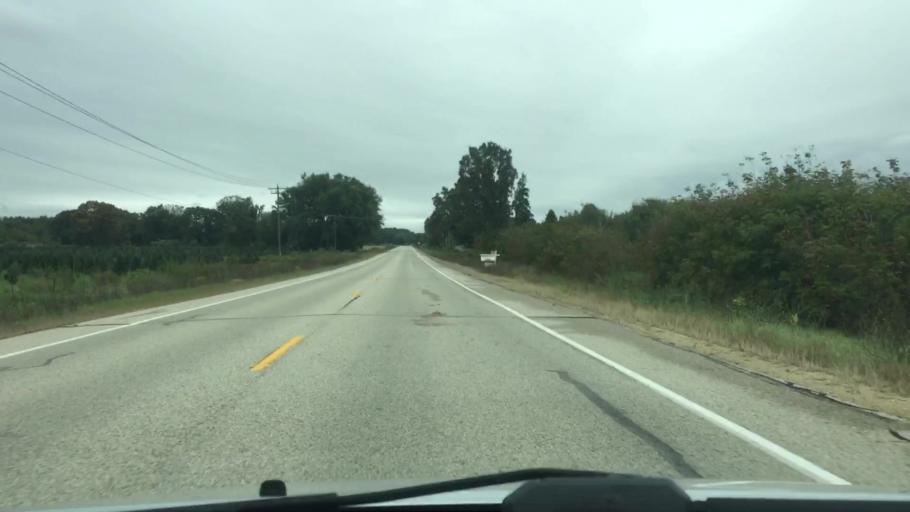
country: US
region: Wisconsin
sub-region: Jefferson County
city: Palmyra
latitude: 42.8239
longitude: -88.5553
